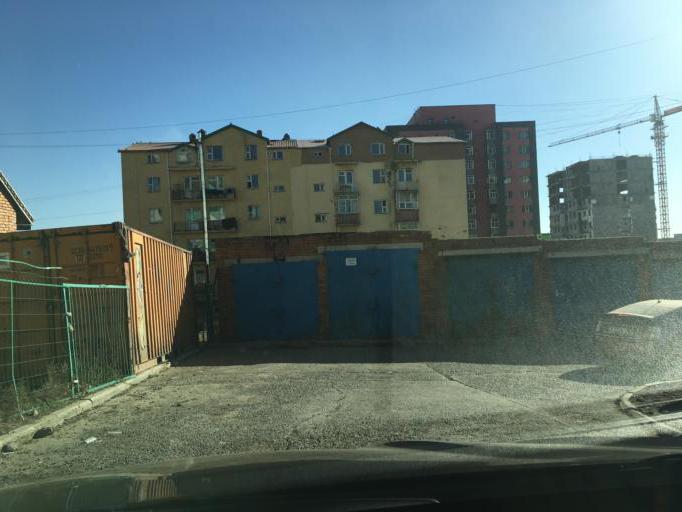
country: MN
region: Ulaanbaatar
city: Ulaanbaatar
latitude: 47.9256
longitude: 106.8681
